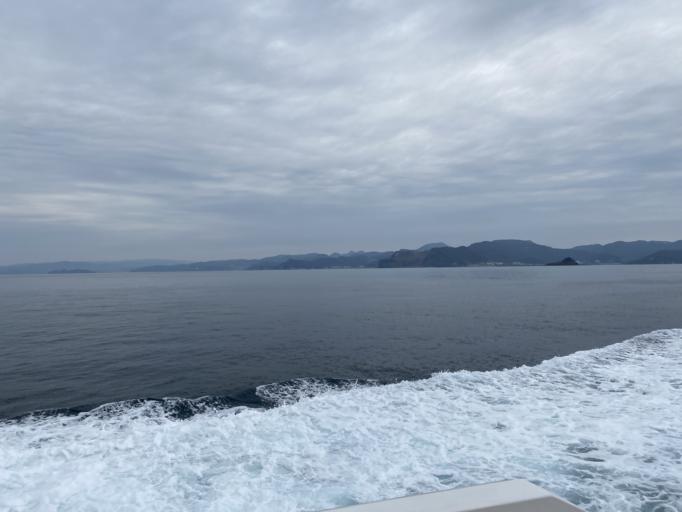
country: JP
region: Nagasaki
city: Nagasaki-shi
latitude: 32.7052
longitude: 129.7950
